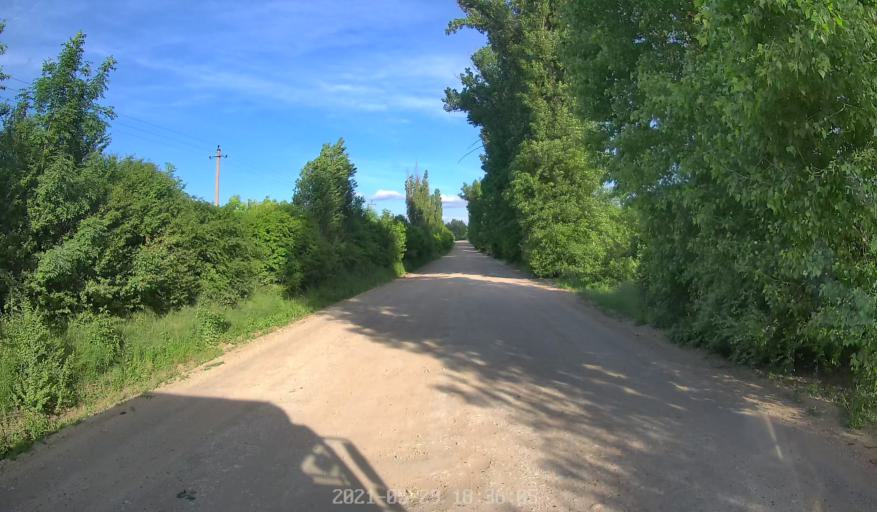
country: MD
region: Chisinau
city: Singera
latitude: 46.8077
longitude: 28.9227
